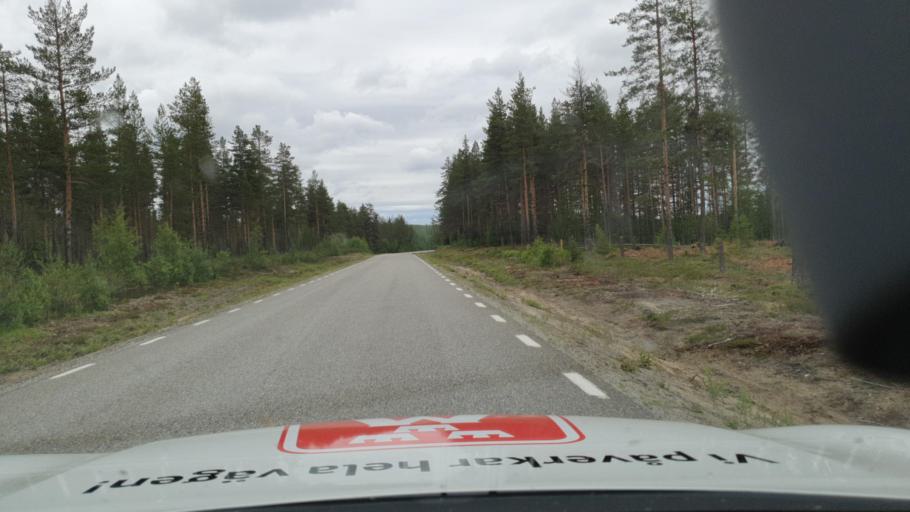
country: SE
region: Vaesterbotten
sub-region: Lycksele Kommun
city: Lycksele
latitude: 64.2037
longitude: 18.2914
